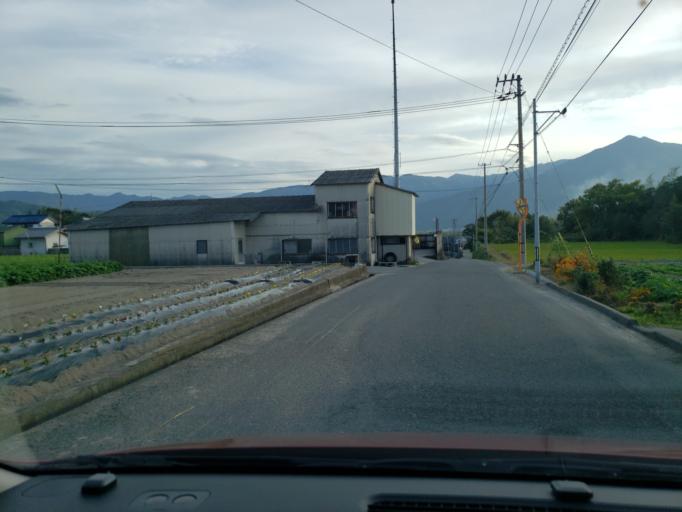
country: JP
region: Tokushima
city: Wakimachi
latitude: 34.0787
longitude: 134.2283
